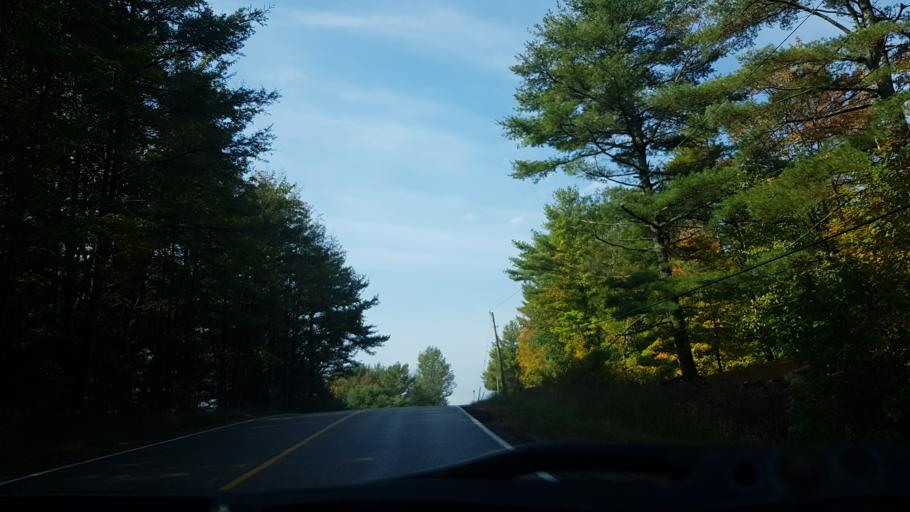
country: CA
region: Ontario
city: Gravenhurst
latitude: 44.7826
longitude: -79.2613
